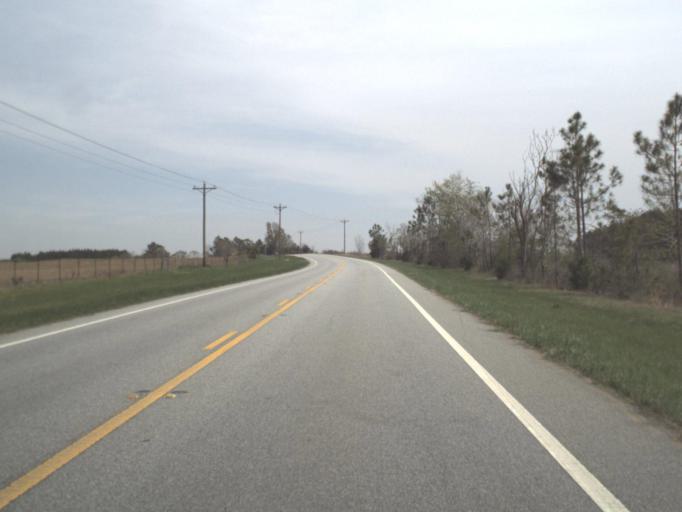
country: US
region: Alabama
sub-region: Geneva County
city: Geneva
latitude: 30.9414
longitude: -85.7872
